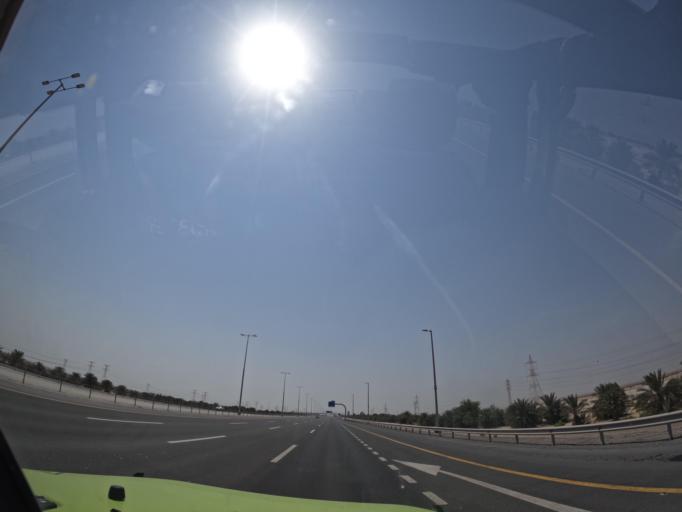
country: AE
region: Abu Dhabi
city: Abu Dhabi
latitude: 24.1725
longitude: 54.3650
